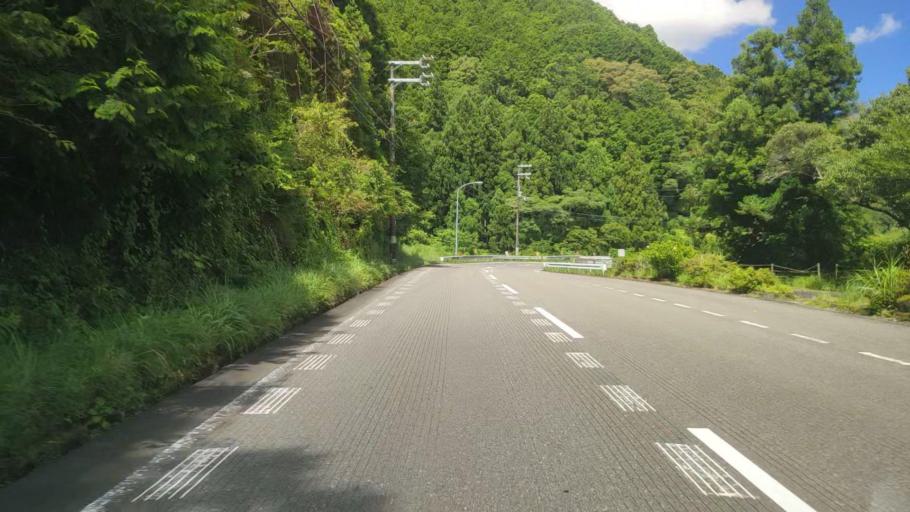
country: JP
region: Wakayama
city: Shingu
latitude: 33.8103
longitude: 135.8631
